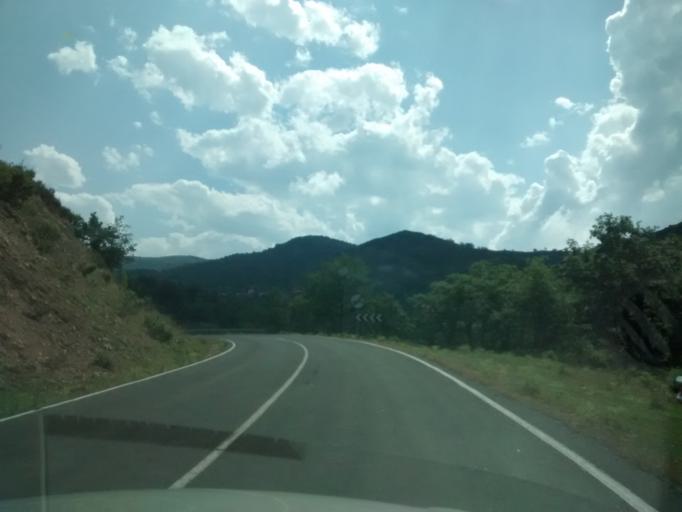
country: ES
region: La Rioja
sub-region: Provincia de La Rioja
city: Rabanera
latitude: 42.1959
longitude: -2.4798
